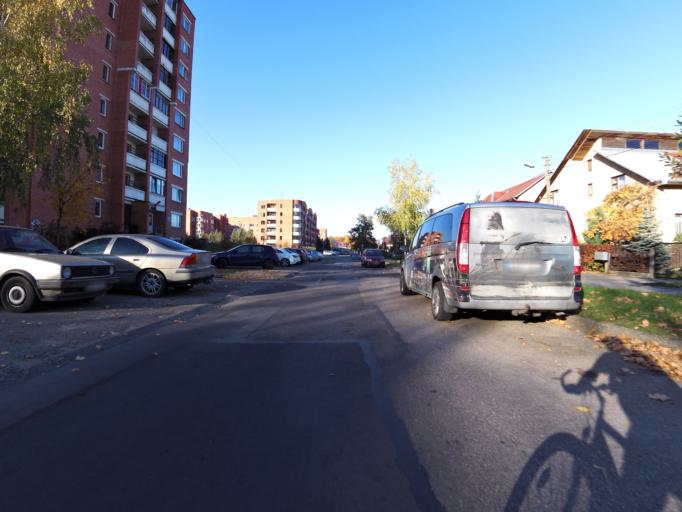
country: LT
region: Vilnius County
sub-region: Vilnius
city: Fabijoniskes
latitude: 54.7429
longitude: 25.2724
